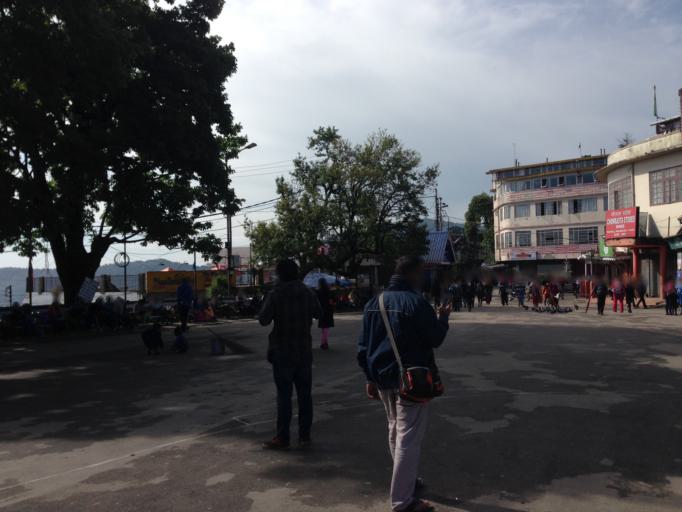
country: IN
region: West Bengal
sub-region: Darjiling
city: Darjiling
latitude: 27.0448
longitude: 88.2677
